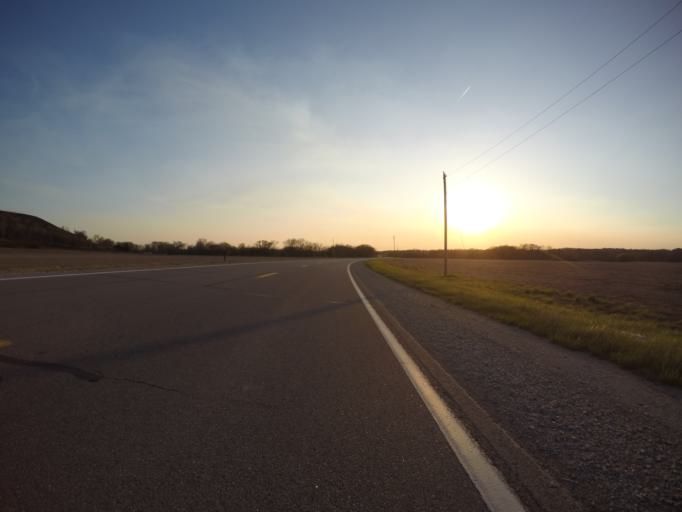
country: US
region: Kansas
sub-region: Riley County
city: Ogden
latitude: 39.1036
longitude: -96.6383
